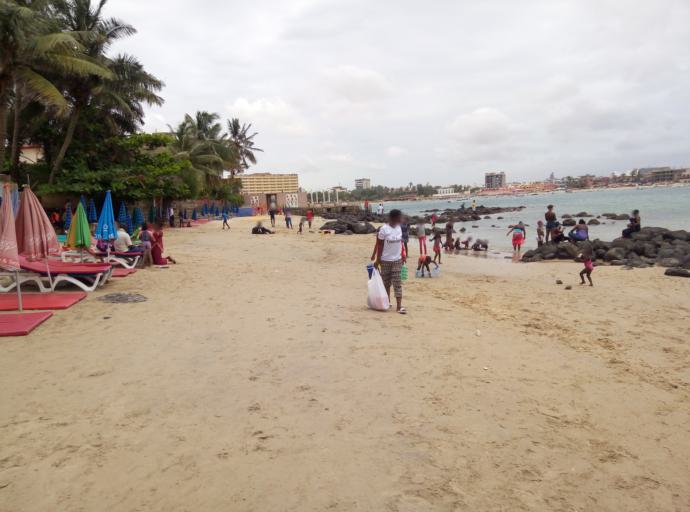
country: SN
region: Dakar
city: Mermoz Boabab
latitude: 14.7551
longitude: -17.5139
